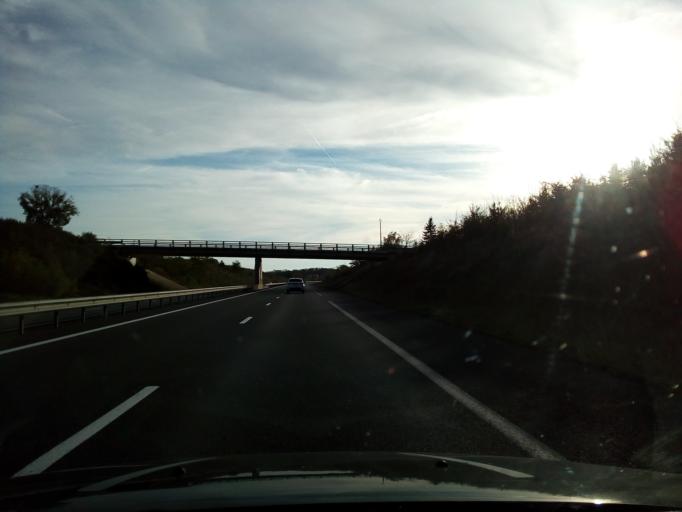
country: FR
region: Poitou-Charentes
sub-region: Departement de la Charente
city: Taponnat-Fleurignac
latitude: 45.7639
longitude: 0.3959
